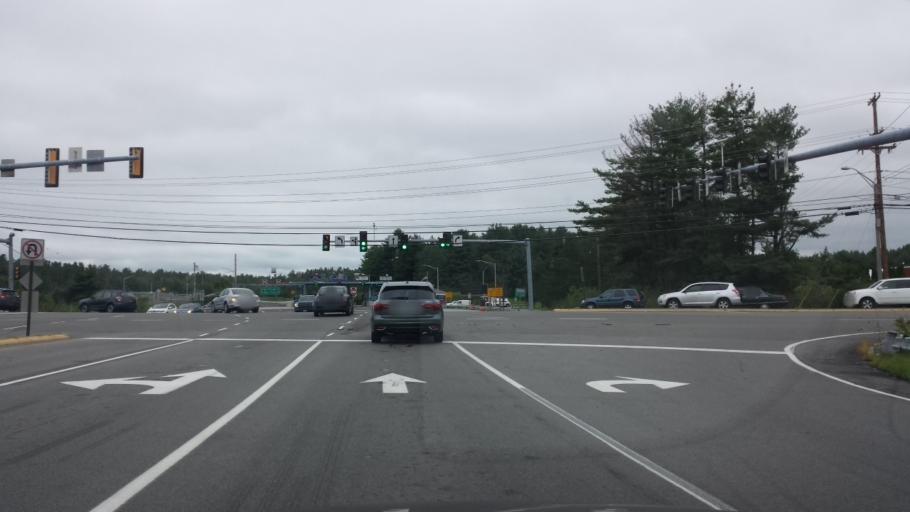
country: US
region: Maine
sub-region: York County
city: Biddeford
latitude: 43.4776
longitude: -70.4958
